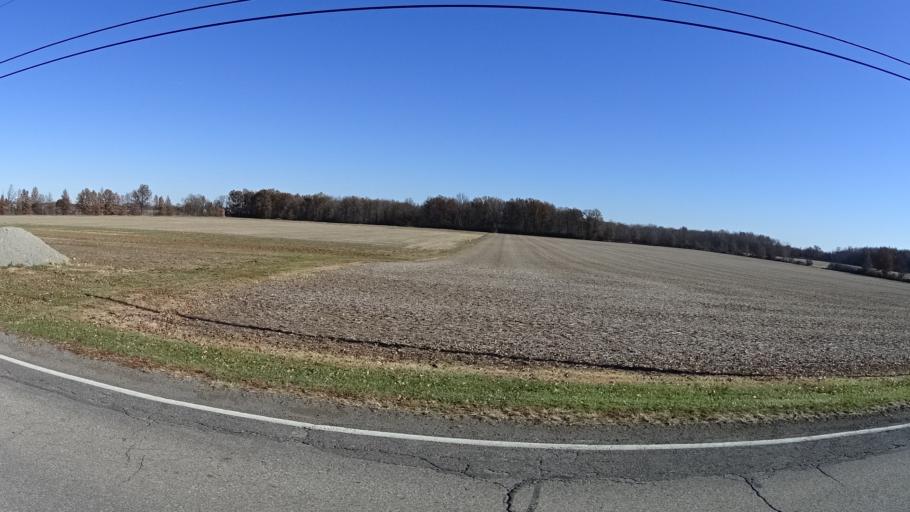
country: US
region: Ohio
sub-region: Lorain County
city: Elyria
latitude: 41.3269
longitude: -82.1521
